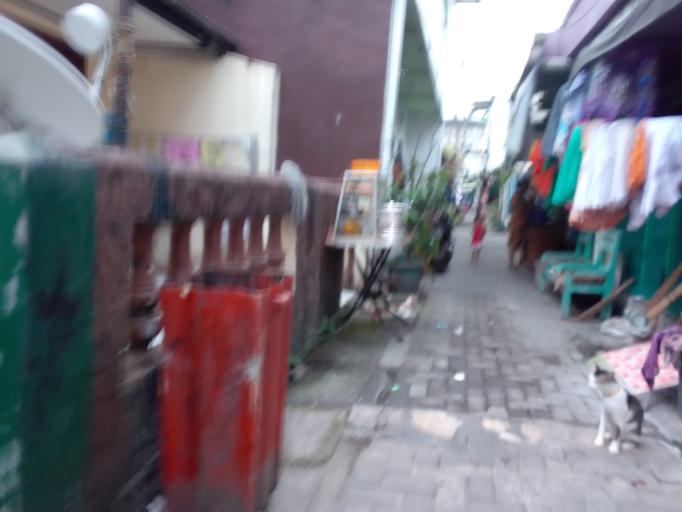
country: ID
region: Jakarta Raya
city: Jakarta
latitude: -6.1652
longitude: 106.8064
